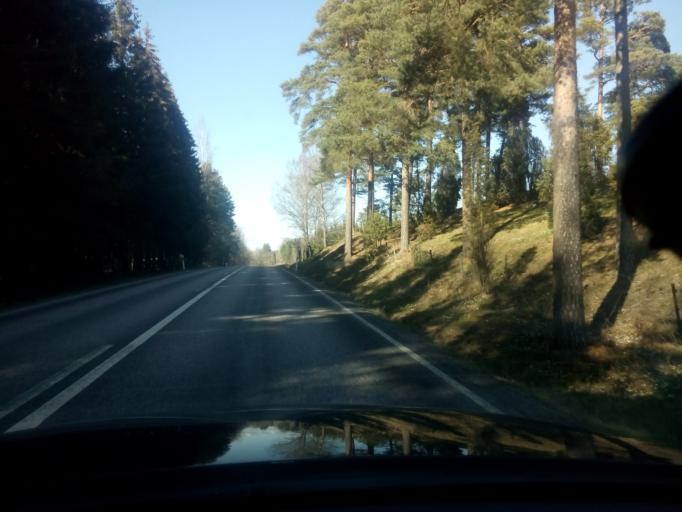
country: SE
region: Soedermanland
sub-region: Flens Kommun
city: Malmkoping
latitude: 58.9972
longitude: 16.8443
